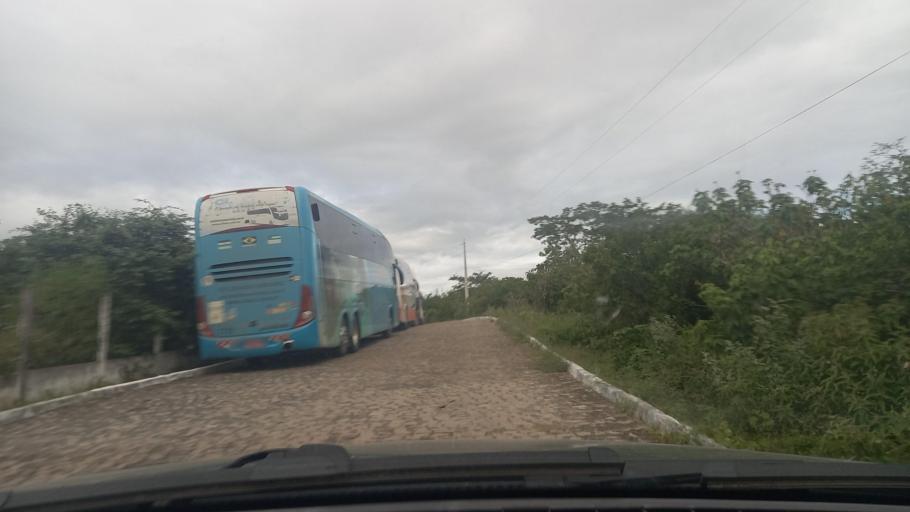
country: BR
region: Sergipe
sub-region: Caninde De Sao Francisco
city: Caninde de Sao Francisco
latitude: -9.6184
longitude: -37.8110
